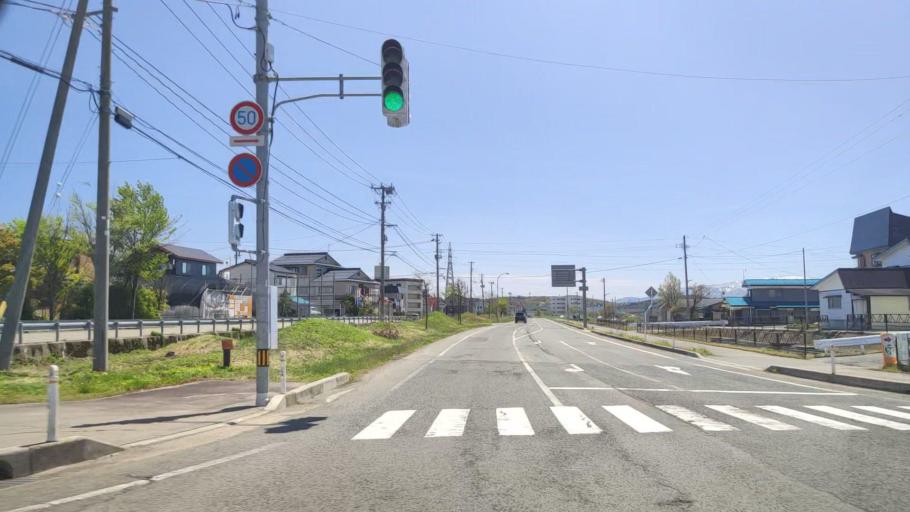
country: JP
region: Yamagata
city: Shinjo
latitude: 38.7500
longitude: 140.2954
